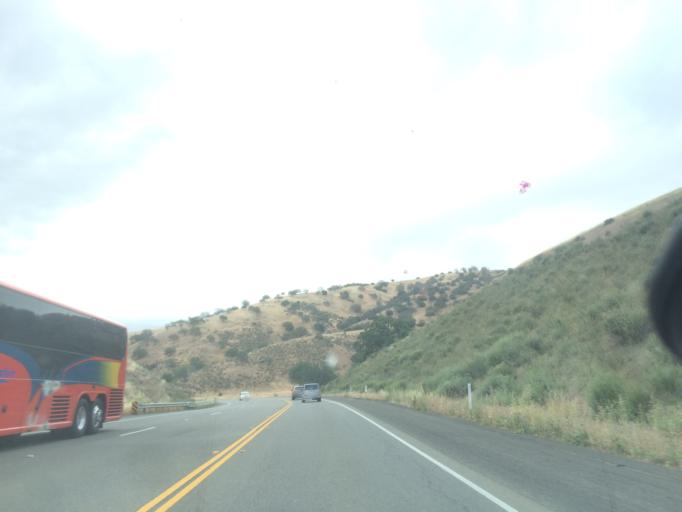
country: US
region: California
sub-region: San Luis Obispo County
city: Shandon
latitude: 35.7753
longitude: -120.1818
